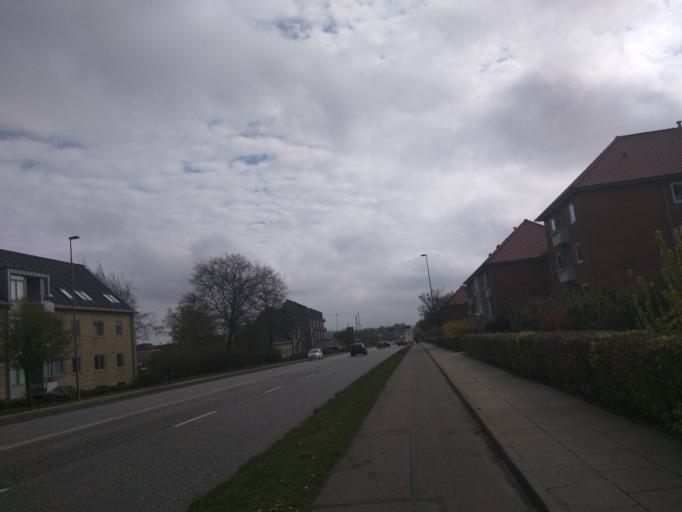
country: DK
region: Central Jutland
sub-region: Viborg Kommune
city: Viborg
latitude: 56.4522
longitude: 9.3921
